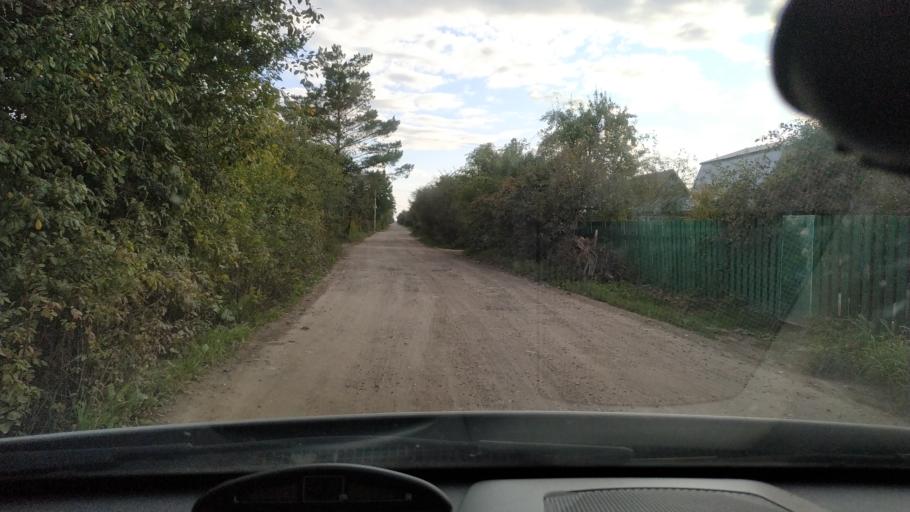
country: RU
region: Rjazan
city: Polyany
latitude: 54.5584
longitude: 39.8771
